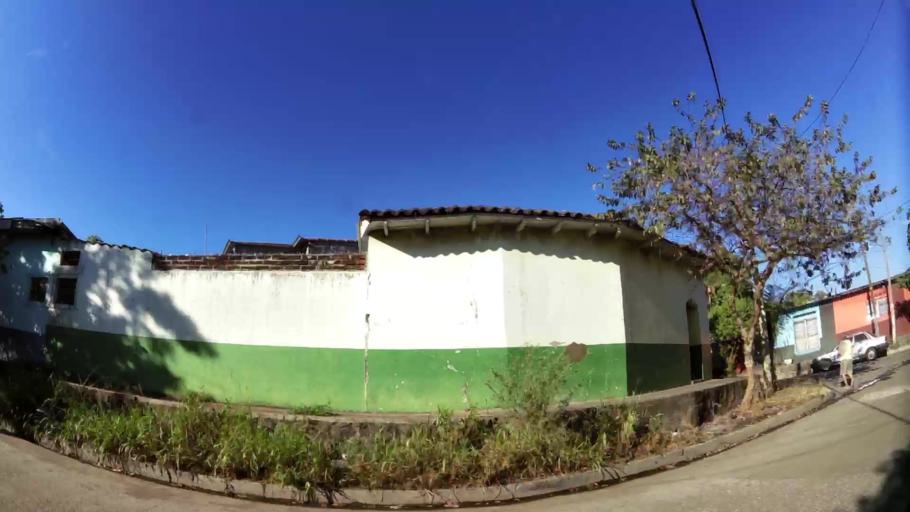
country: SV
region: Sonsonate
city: Sonsonate
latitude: 13.7167
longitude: -89.7190
